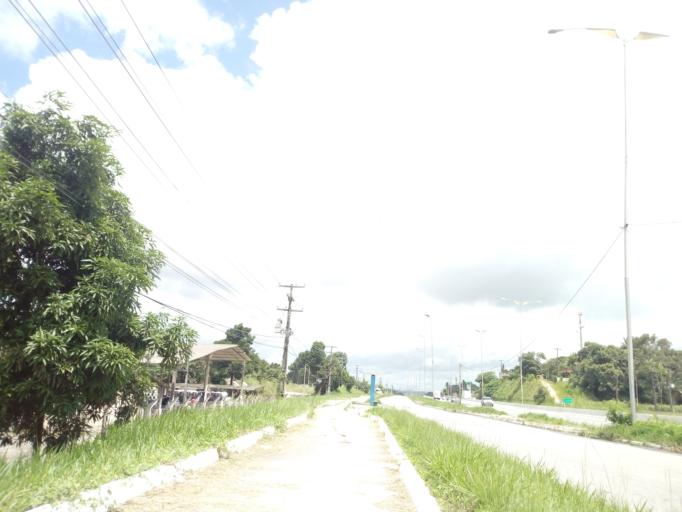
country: BR
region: Pernambuco
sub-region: Cabo De Santo Agostinho
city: Cabo
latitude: -8.2694
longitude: -35.0216
